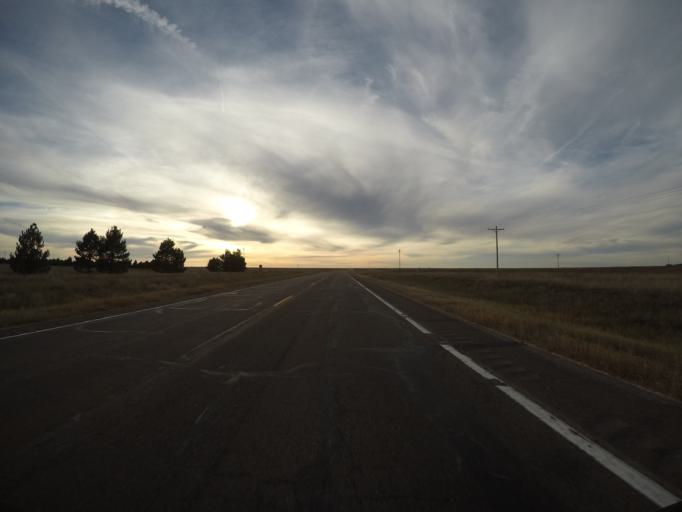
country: US
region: Colorado
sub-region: Yuma County
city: Yuma
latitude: 39.6698
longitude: -102.9151
